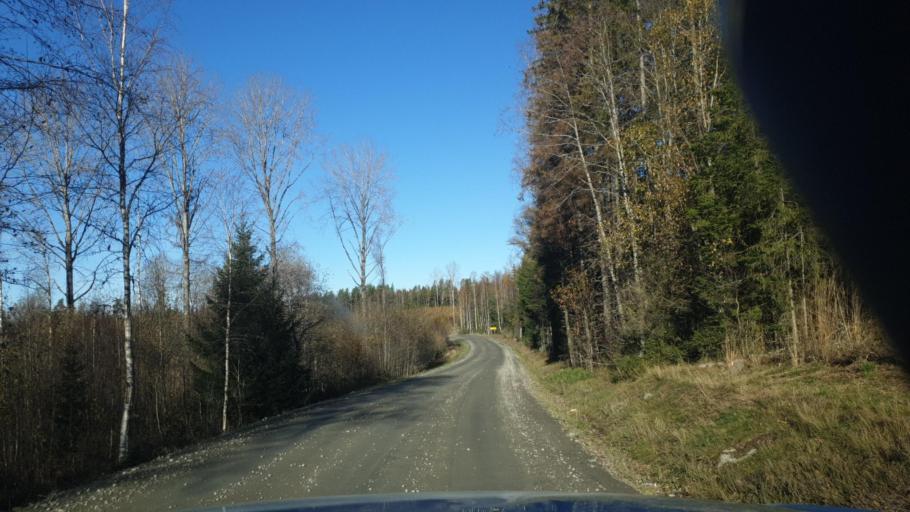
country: SE
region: Vaermland
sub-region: Karlstads Kommun
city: Edsvalla
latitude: 59.4797
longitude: 13.0753
